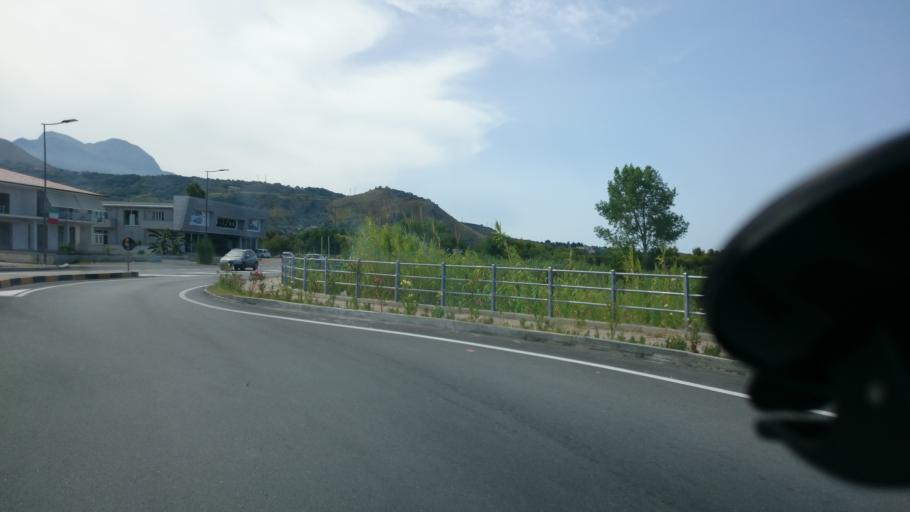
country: IT
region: Calabria
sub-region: Provincia di Cosenza
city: Santa Maria del Cedro
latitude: 39.7311
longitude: 15.8100
